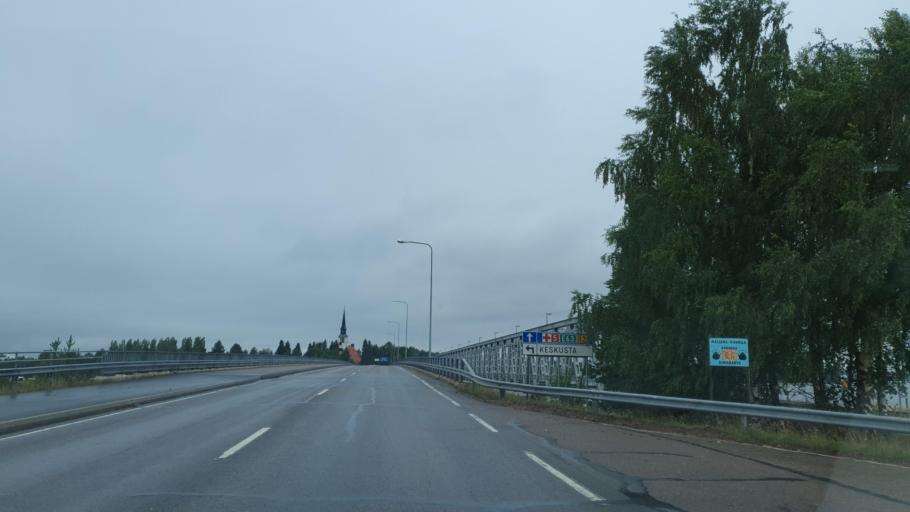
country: FI
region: Lapland
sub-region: Itae-Lappi
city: Kemijaervi
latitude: 66.7159
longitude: 27.4518
